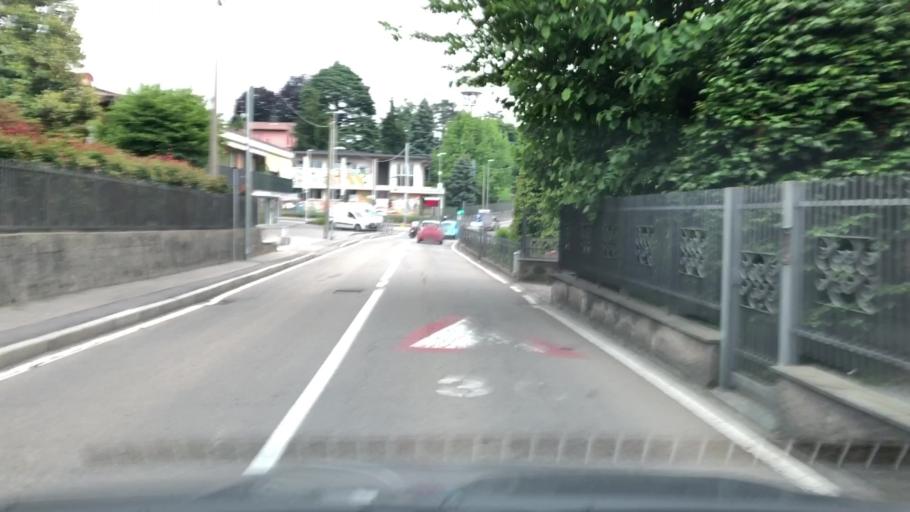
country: IT
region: Lombardy
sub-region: Provincia di Como
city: Casnate Con Bernate
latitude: 45.7616
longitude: 9.0756
